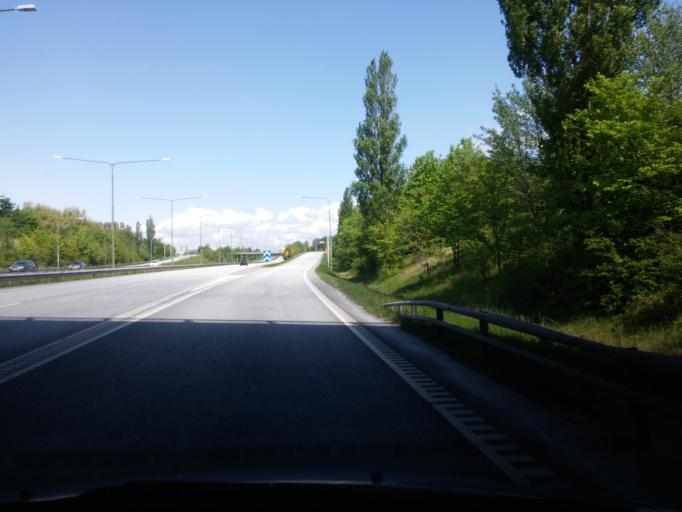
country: SE
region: Skane
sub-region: Malmo
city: Tygelsjo
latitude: 55.5602
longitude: 13.0001
